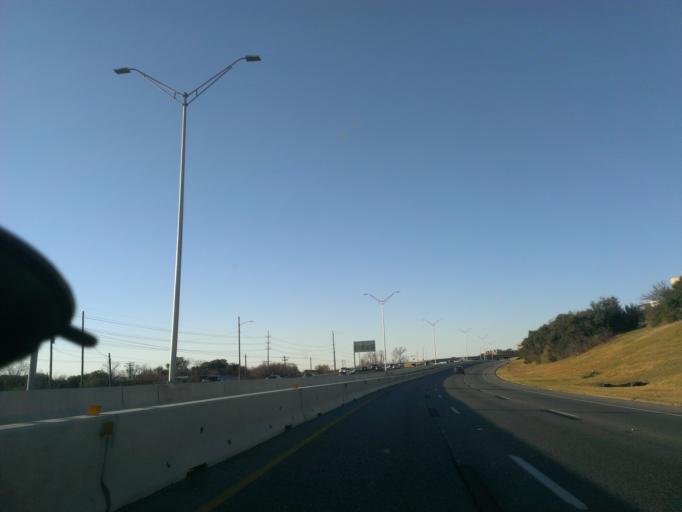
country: US
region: Texas
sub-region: Travis County
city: West Lake Hills
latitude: 30.3564
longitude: -97.7464
